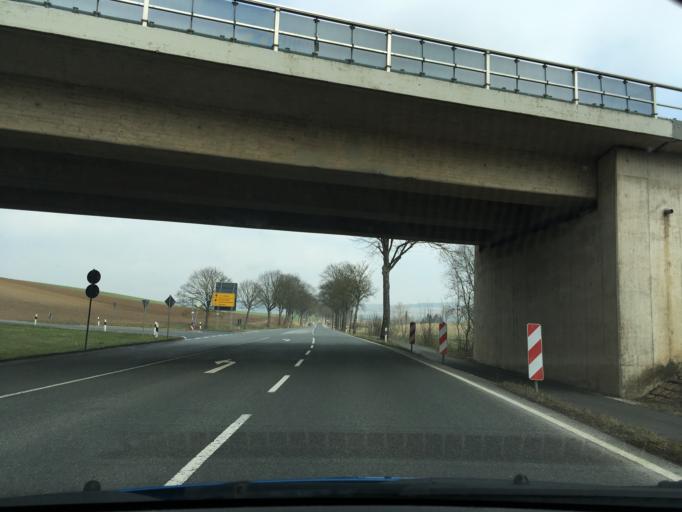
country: DE
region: Lower Saxony
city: Einbeck
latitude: 51.8661
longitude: 9.8750
